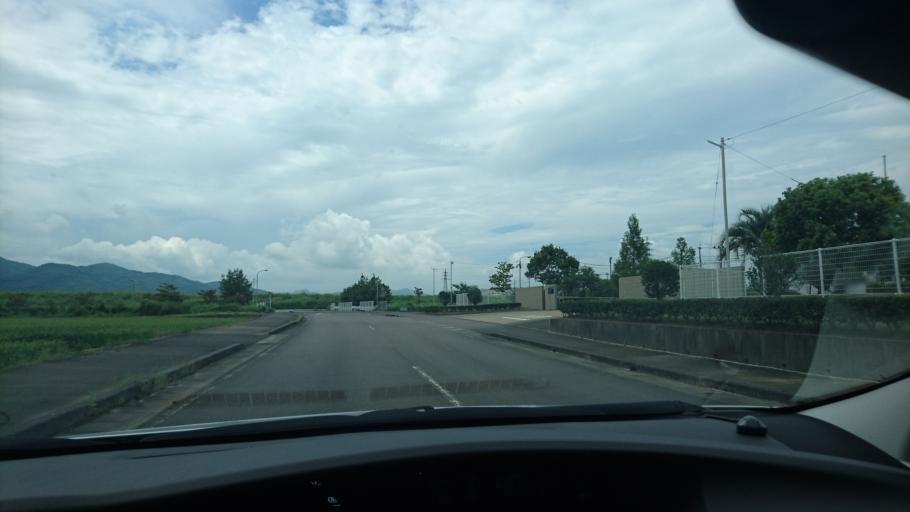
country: JP
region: Saga Prefecture
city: Takeocho-takeo
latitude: 33.2103
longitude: 130.1131
